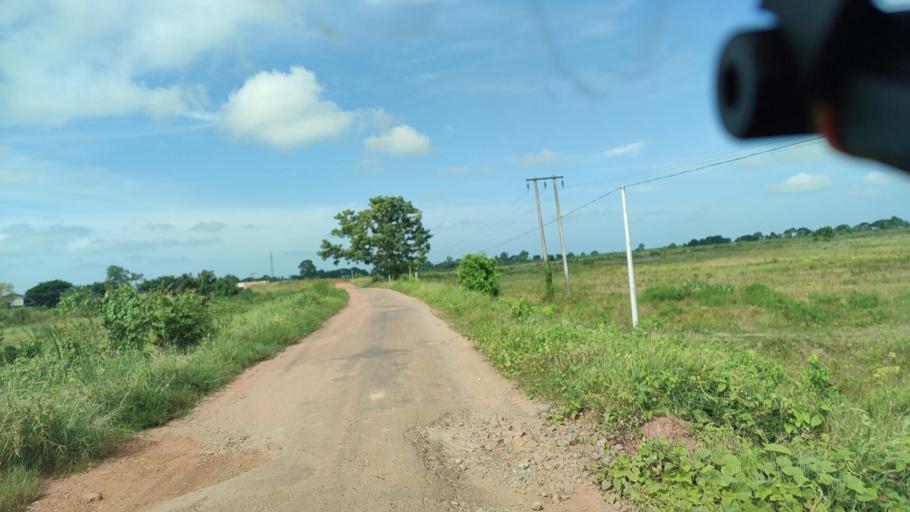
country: MM
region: Bago
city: Letpandan
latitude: 17.7304
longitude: 95.6093
